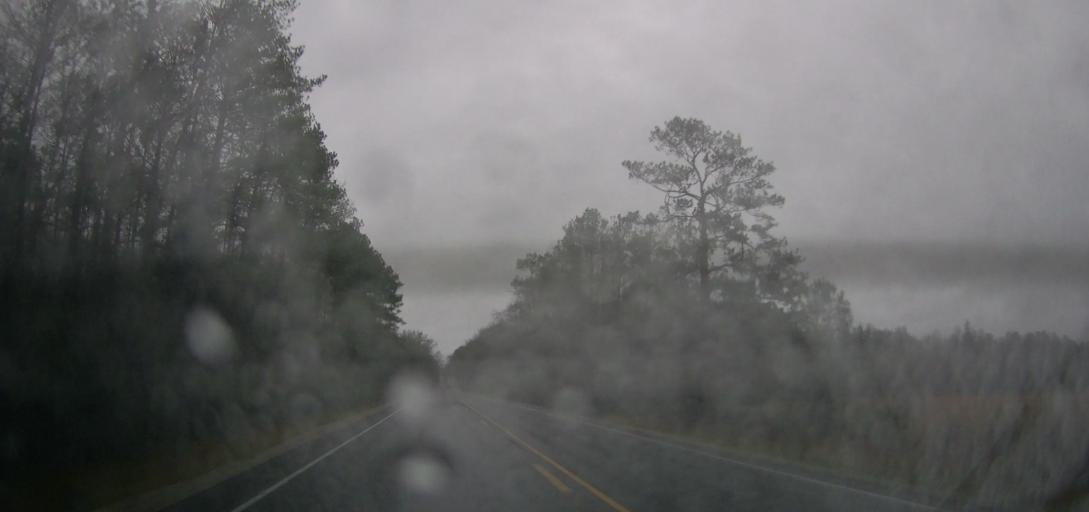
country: US
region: Alabama
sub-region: Autauga County
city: Pine Level
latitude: 32.5700
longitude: -86.6779
